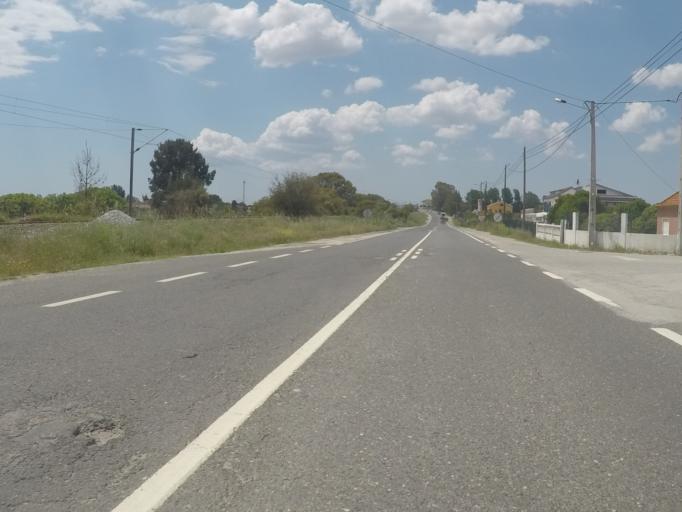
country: PT
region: Setubal
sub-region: Setubal
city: Setubal
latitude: 38.5685
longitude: -8.7639
